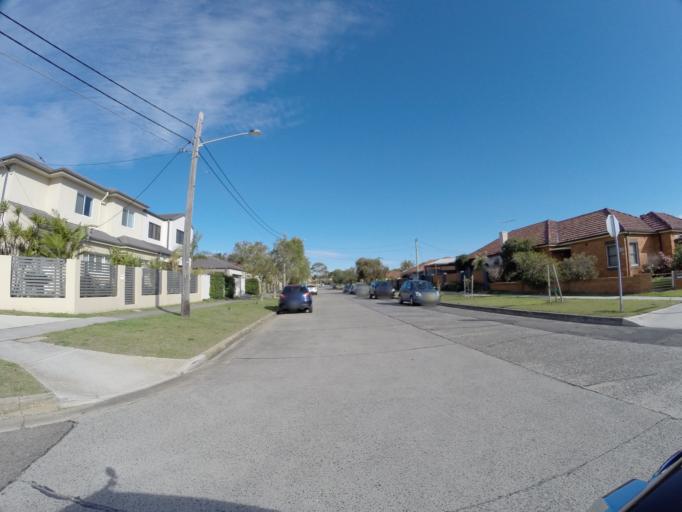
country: AU
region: New South Wales
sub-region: Randwick
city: South Coogee
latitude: -33.9344
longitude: 151.2460
